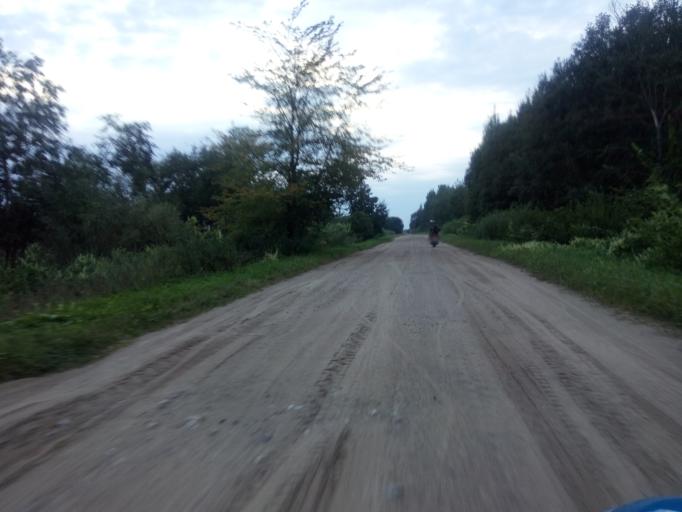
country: BY
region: Vitebsk
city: Dzisna
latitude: 55.6720
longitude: 28.3090
